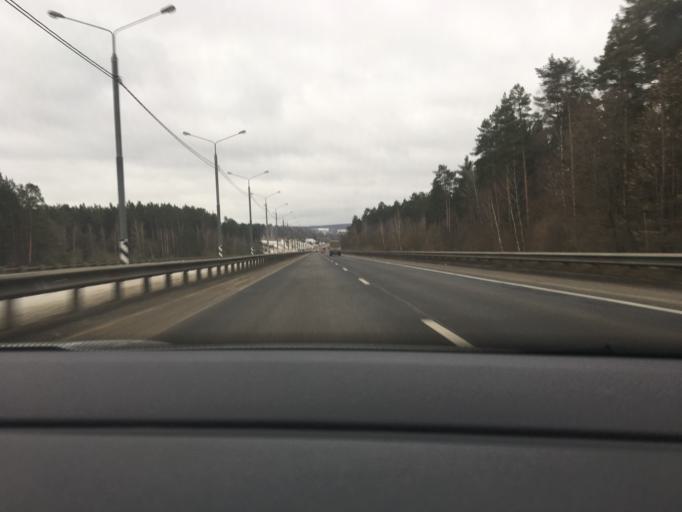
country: RU
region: Tula
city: Zaokskiy
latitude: 54.7807
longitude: 37.4880
